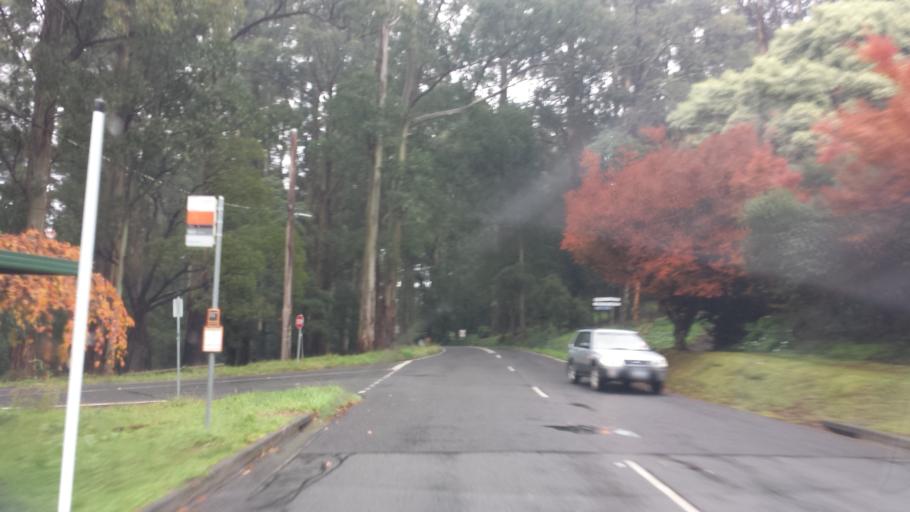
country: AU
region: Victoria
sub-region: Yarra Ranges
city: Kallista
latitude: -37.8865
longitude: 145.3781
